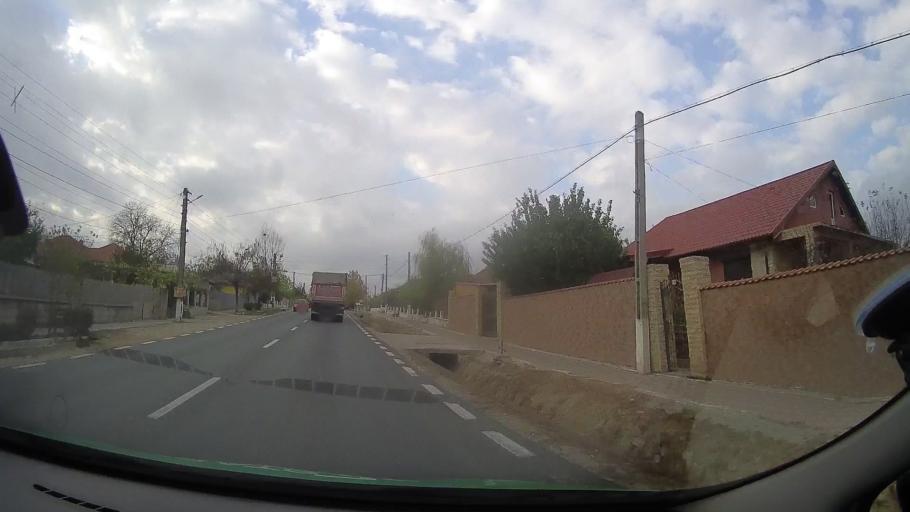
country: RO
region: Constanta
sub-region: Comuna Mircea Voda
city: Satu Nou
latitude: 44.2683
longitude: 28.2229
